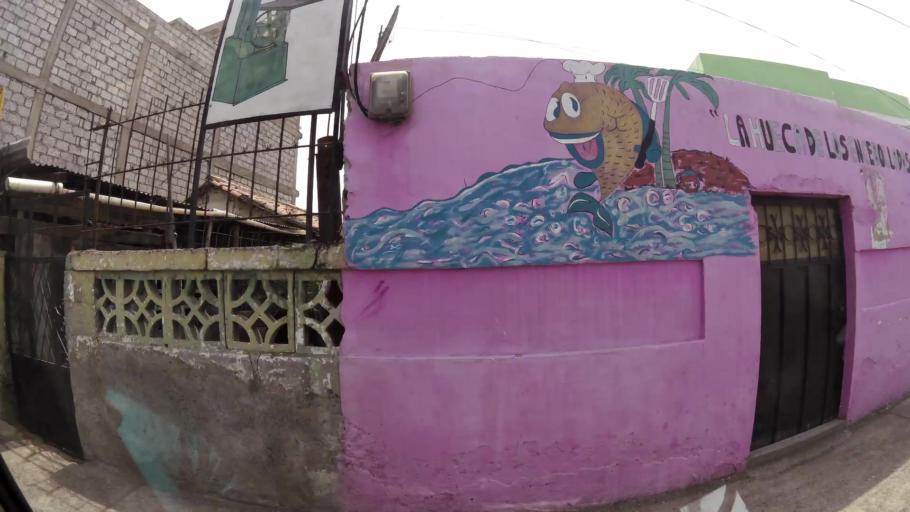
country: EC
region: Cotopaxi
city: San Miguel de Salcedo
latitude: -1.0486
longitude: -78.5941
